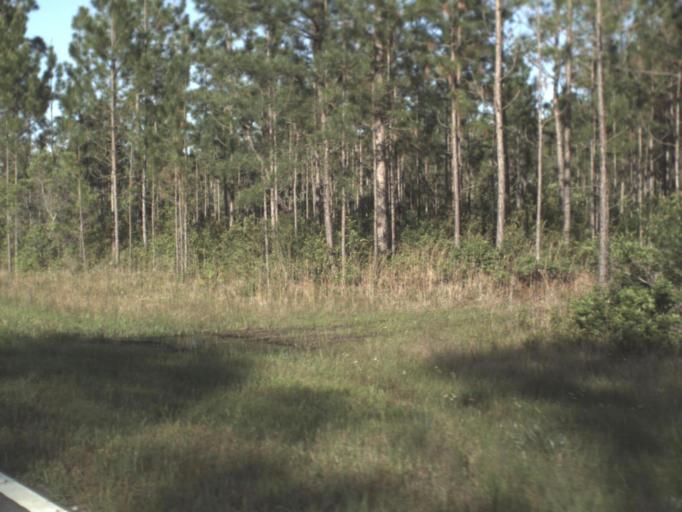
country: US
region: Florida
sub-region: Liberty County
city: Bristol
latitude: 30.2439
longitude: -84.8683
